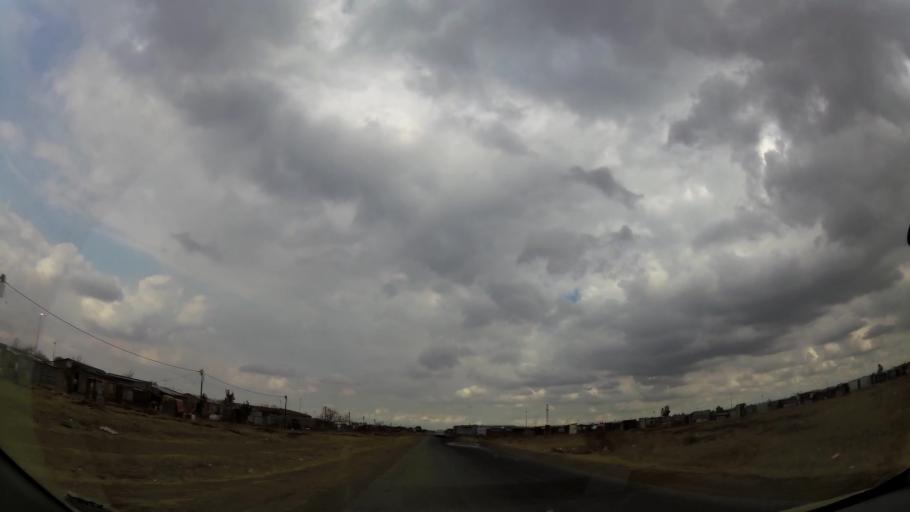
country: ZA
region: Orange Free State
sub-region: Fezile Dabi District Municipality
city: Sasolburg
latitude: -26.8596
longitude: 27.8725
